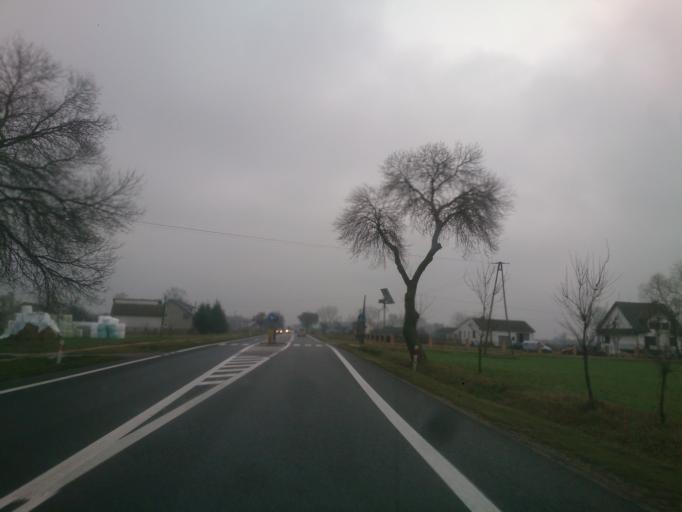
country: PL
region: Masovian Voivodeship
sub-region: Powiat sierpecki
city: Zawidz
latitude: 52.8124
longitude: 19.8083
